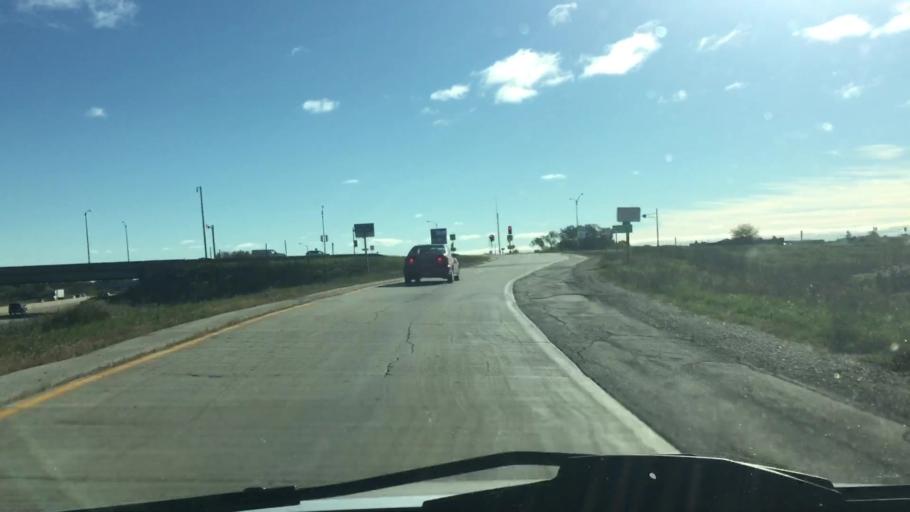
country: US
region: Wisconsin
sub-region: Waukesha County
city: Pewaukee
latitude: 43.0461
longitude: -88.2578
